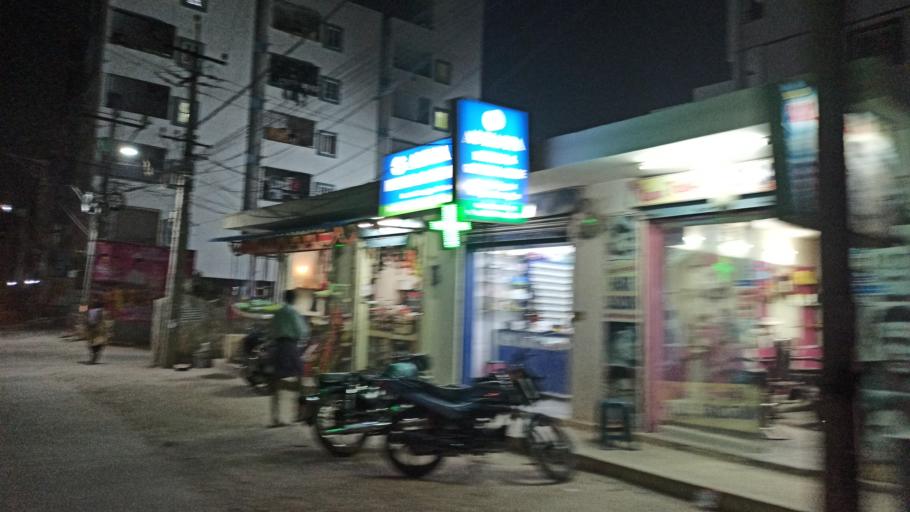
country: IN
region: Telangana
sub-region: Rangareddi
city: Kukatpalli
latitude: 17.5226
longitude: 78.3894
